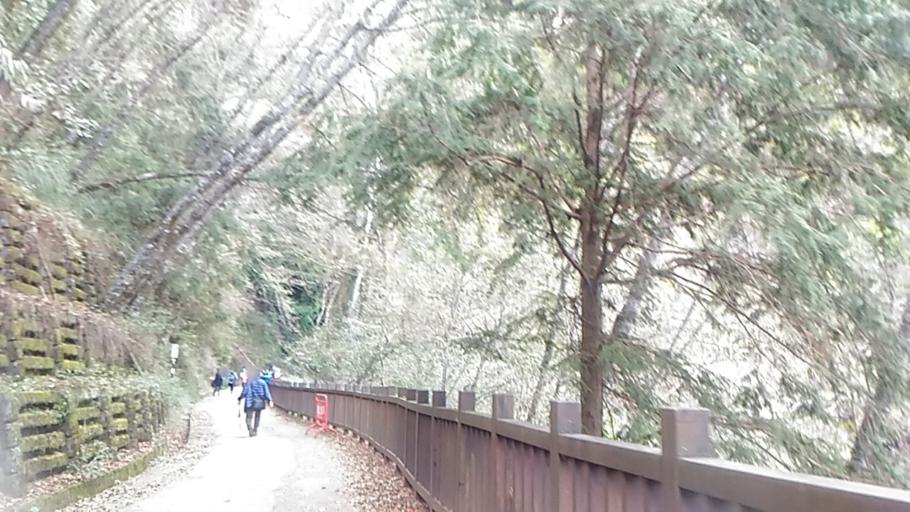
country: TW
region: Taiwan
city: Daxi
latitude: 24.4127
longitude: 121.3026
